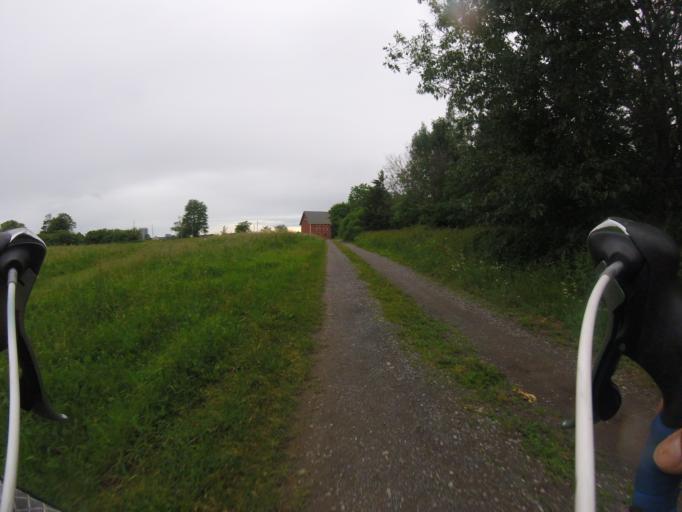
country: CA
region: Ontario
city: Ottawa
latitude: 45.3854
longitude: -75.7046
